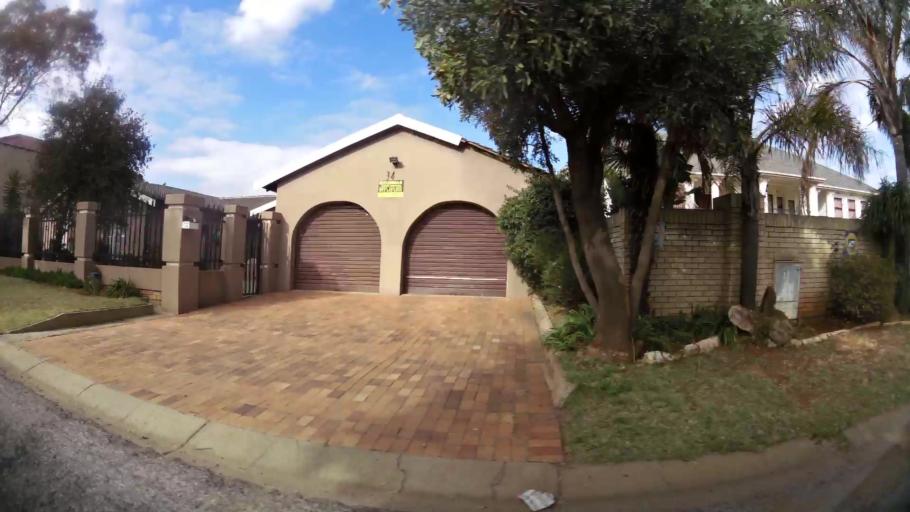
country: ZA
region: Gauteng
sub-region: City of Johannesburg Metropolitan Municipality
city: Roodepoort
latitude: -26.2030
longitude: 27.9168
